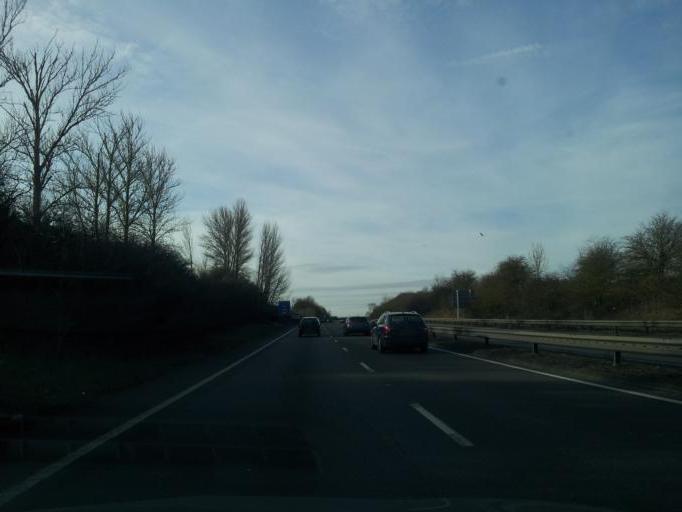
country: GB
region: England
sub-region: Cambridgeshire
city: Little Paxton
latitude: 52.2406
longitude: -0.2797
